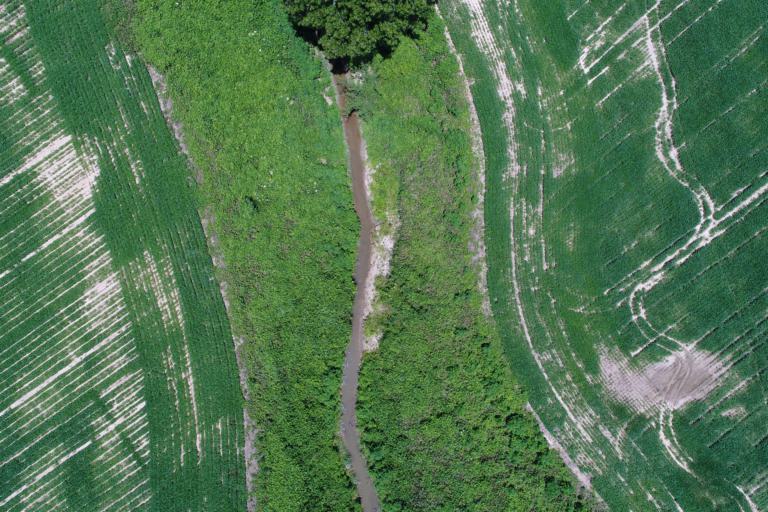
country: US
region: Mississippi
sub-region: De Soto County
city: Walls
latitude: 34.9176
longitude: -90.1359
